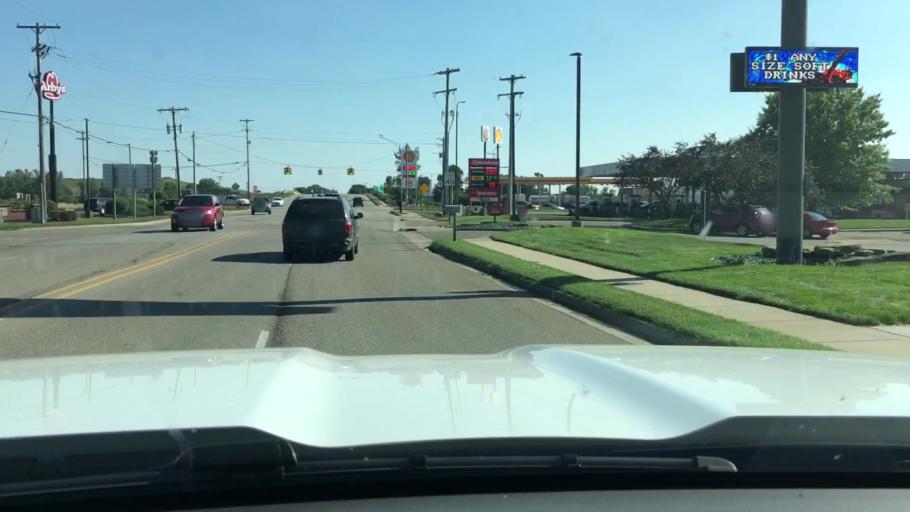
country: US
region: Michigan
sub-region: Ottawa County
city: Coopersville
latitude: 43.0589
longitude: -85.9569
